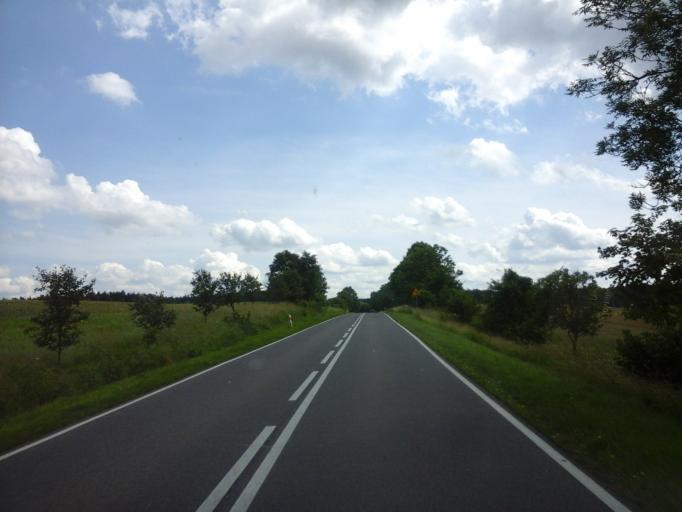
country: PL
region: West Pomeranian Voivodeship
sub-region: Powiat swidwinski
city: Slawoborze
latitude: 53.8516
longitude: 15.7342
